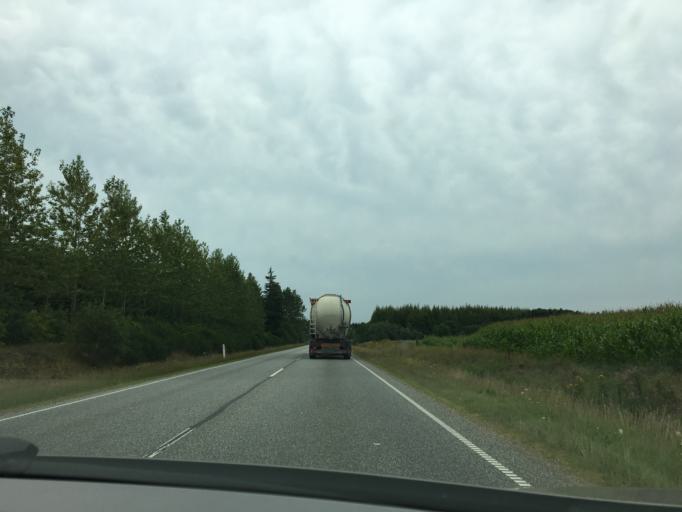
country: DK
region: Central Jutland
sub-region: Herning Kommune
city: Sunds
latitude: 56.3388
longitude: 8.9809
